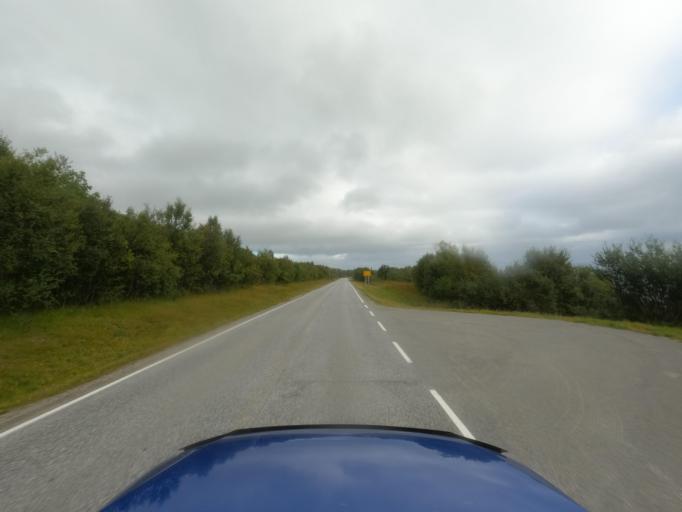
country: NO
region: Finnmark Fylke
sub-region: Porsanger
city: Lakselv
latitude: 70.4312
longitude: 25.1785
